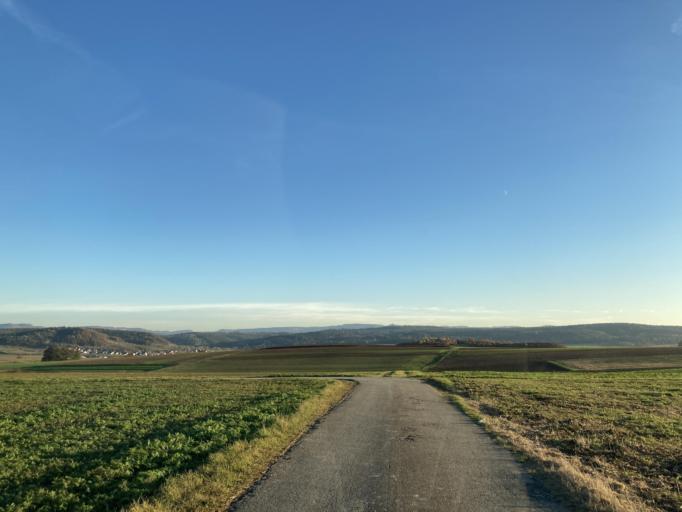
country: DE
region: Baden-Wuerttemberg
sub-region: Tuebingen Region
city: Hirrlingen
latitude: 48.4345
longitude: 8.8993
